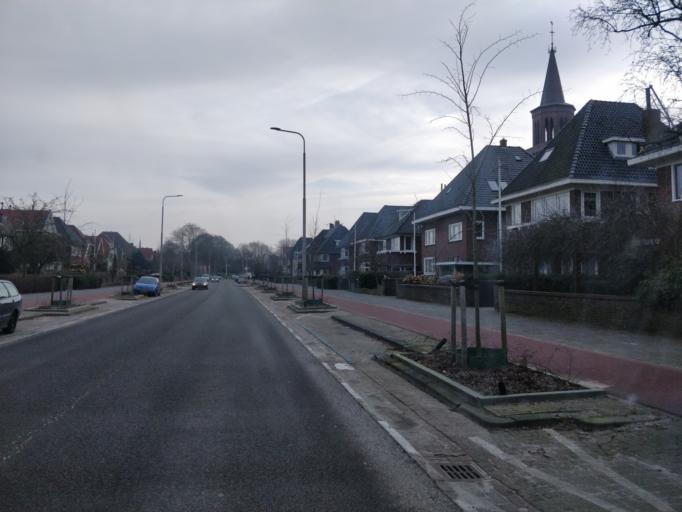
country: NL
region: Friesland
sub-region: Gemeente Leeuwarden
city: Bilgaard
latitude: 53.2044
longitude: 5.7832
